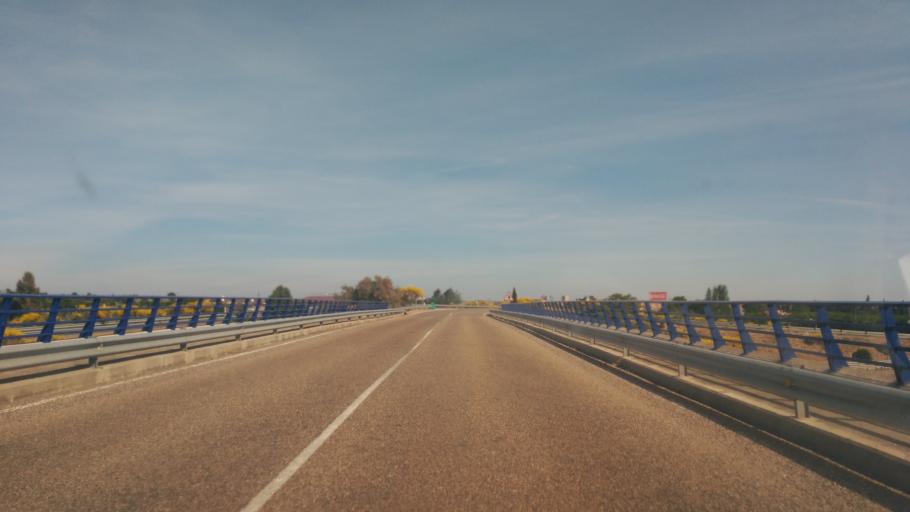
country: ES
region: Castille and Leon
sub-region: Provincia de Zamora
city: Zamora
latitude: 41.4816
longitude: -5.7409
